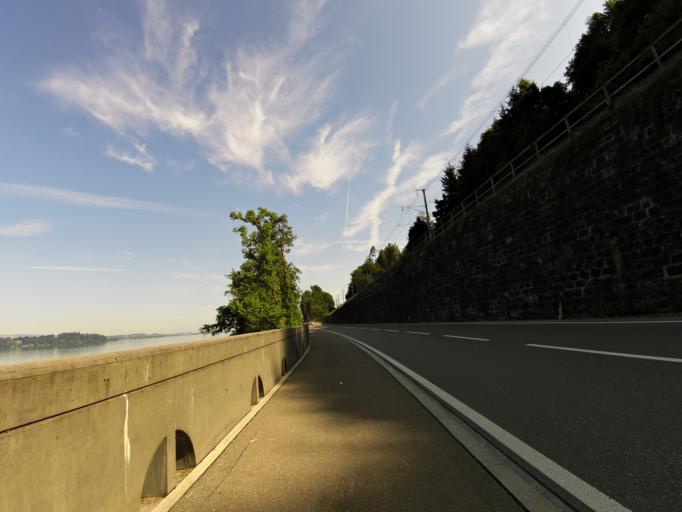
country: CH
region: Zug
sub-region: Zug
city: Walchwil
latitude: 47.1194
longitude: 8.4967
